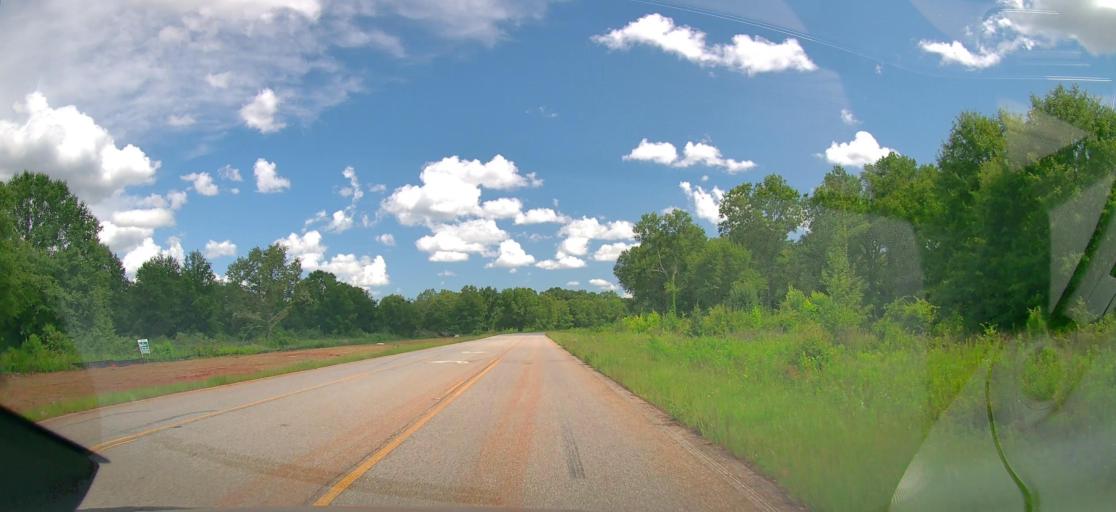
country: US
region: Georgia
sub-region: Peach County
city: Byron
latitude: 32.5976
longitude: -83.7399
